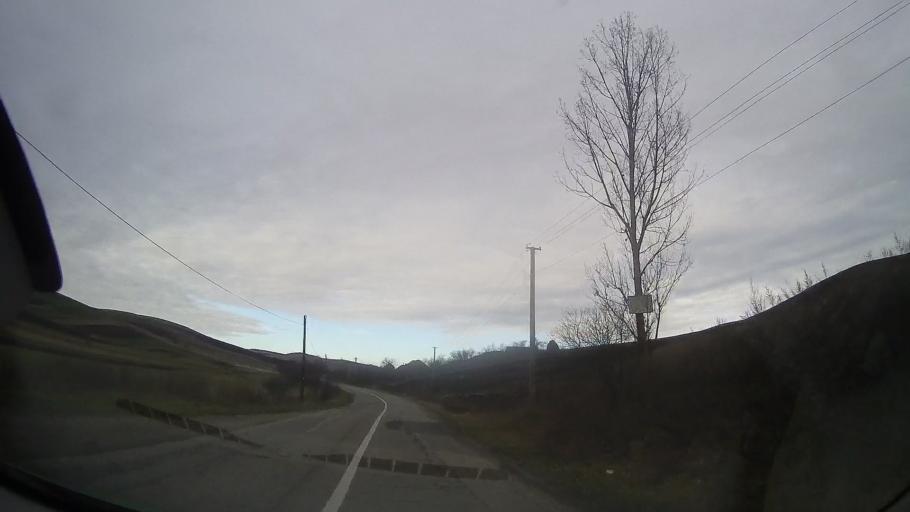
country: RO
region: Cluj
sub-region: Comuna Camarasu
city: Camarasu
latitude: 46.8062
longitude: 24.1456
